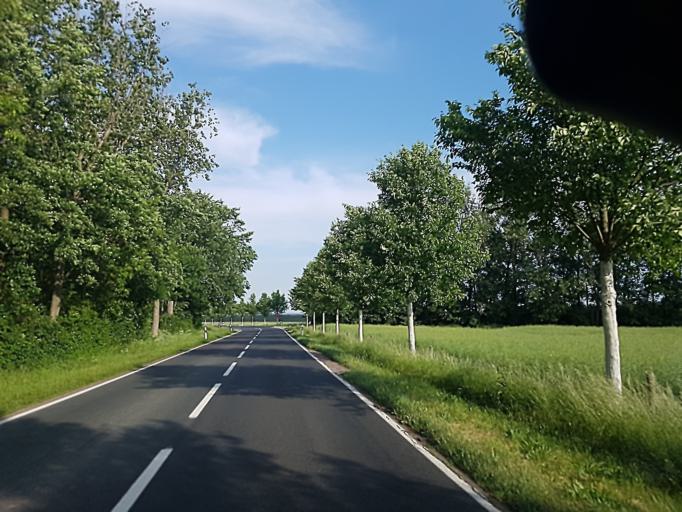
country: DE
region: Brandenburg
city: Niemegk
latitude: 52.0358
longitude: 12.7246
